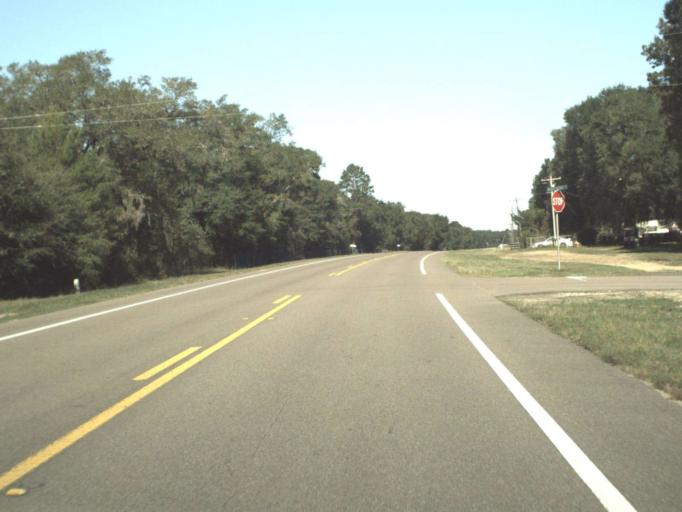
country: US
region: Florida
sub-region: Walton County
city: Freeport
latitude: 30.5818
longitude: -85.9338
